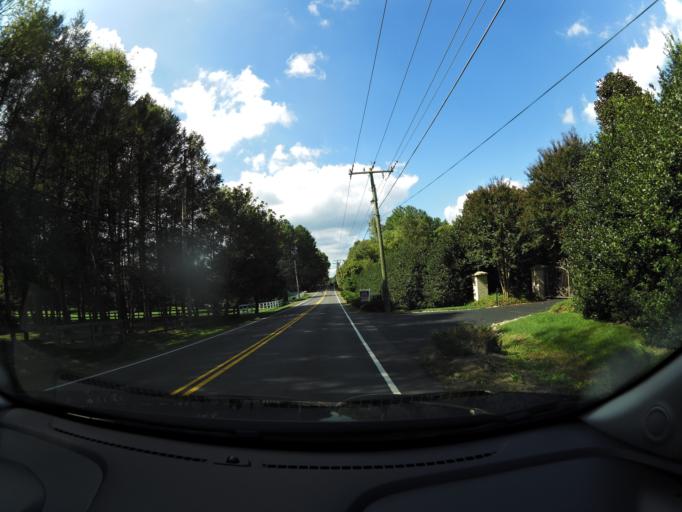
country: US
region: Virginia
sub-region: Fairfax County
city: Great Falls
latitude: 38.9916
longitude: -77.2749
